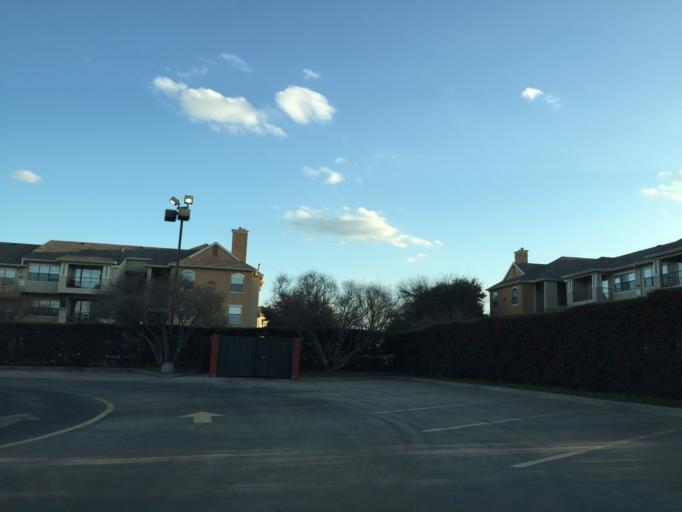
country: US
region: Texas
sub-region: Williamson County
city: Jollyville
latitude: 30.4418
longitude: -97.7471
